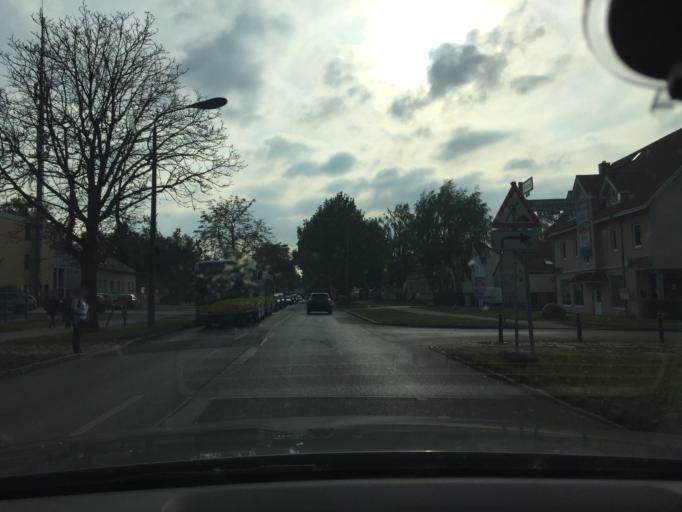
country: DE
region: Berlin
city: Karow
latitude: 52.6118
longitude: 13.4829
